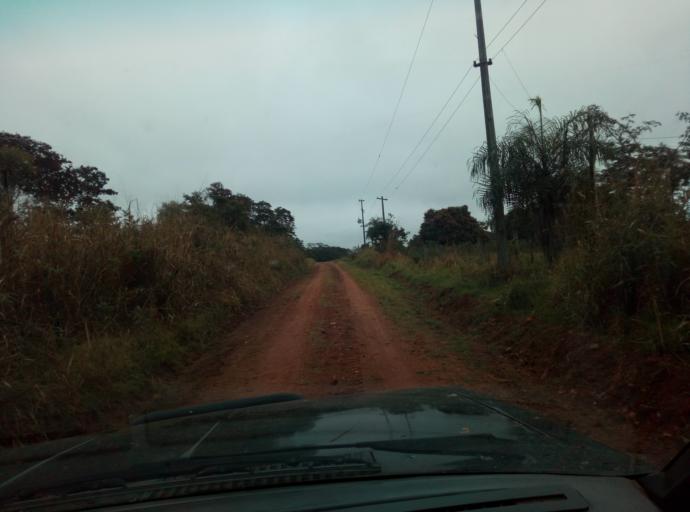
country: PY
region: Caaguazu
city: Carayao
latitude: -25.1904
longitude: -56.3564
